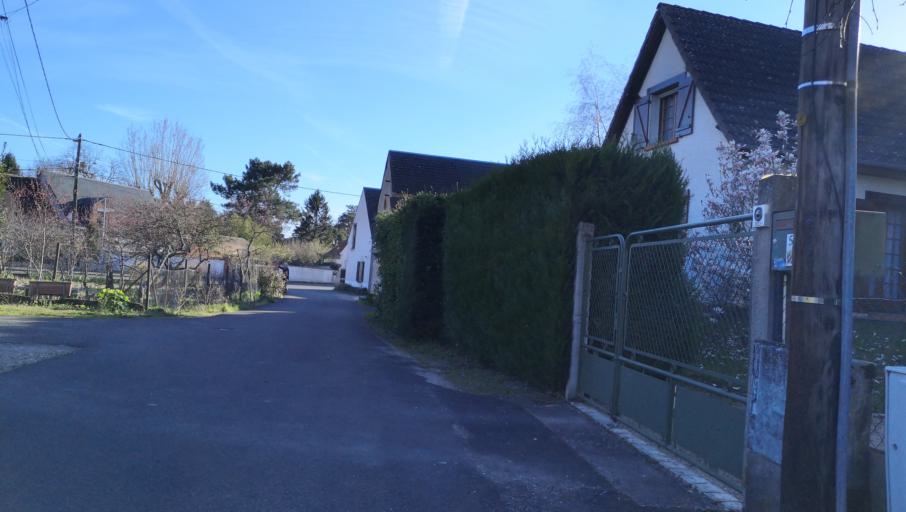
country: FR
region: Centre
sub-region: Departement du Loiret
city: Saint-Jean-de-Braye
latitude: 47.9152
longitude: 1.9901
